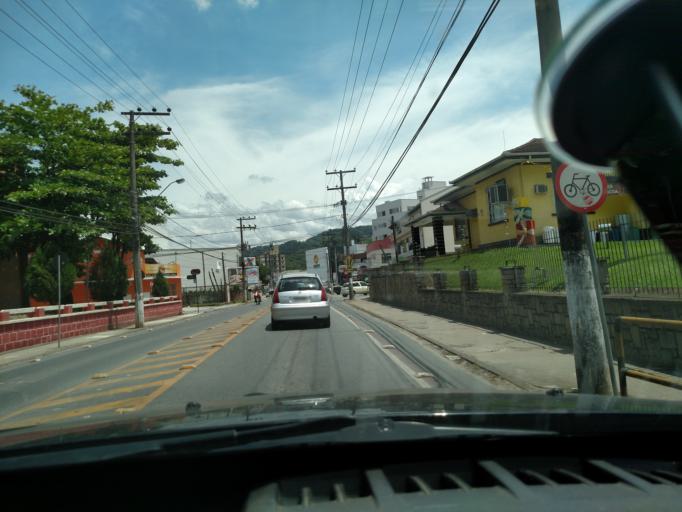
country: BR
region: Santa Catarina
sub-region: Blumenau
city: Blumenau
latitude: -26.9429
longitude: -49.0711
